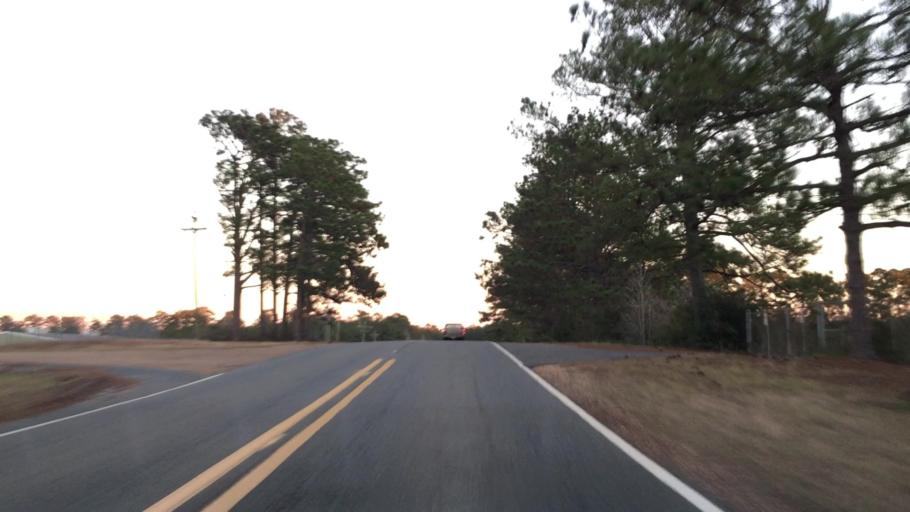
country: US
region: Louisiana
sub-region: Vernon Parish
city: Fort Polk South
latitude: 31.0290
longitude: -93.2040
